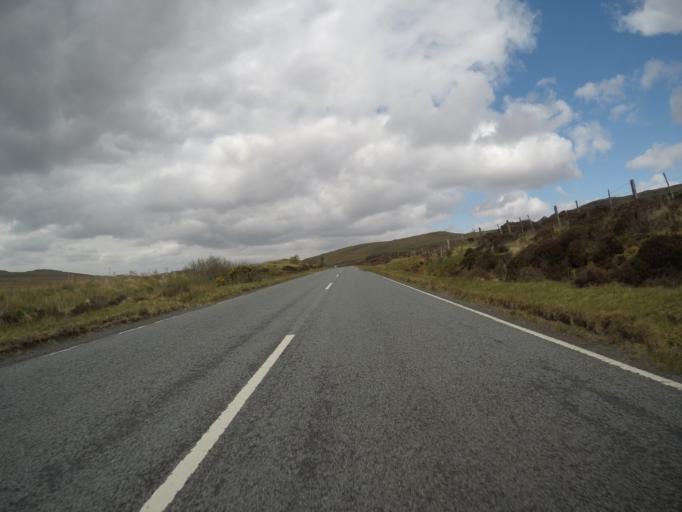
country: GB
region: Scotland
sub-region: Highland
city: Isle of Skye
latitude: 57.3134
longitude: -6.3197
